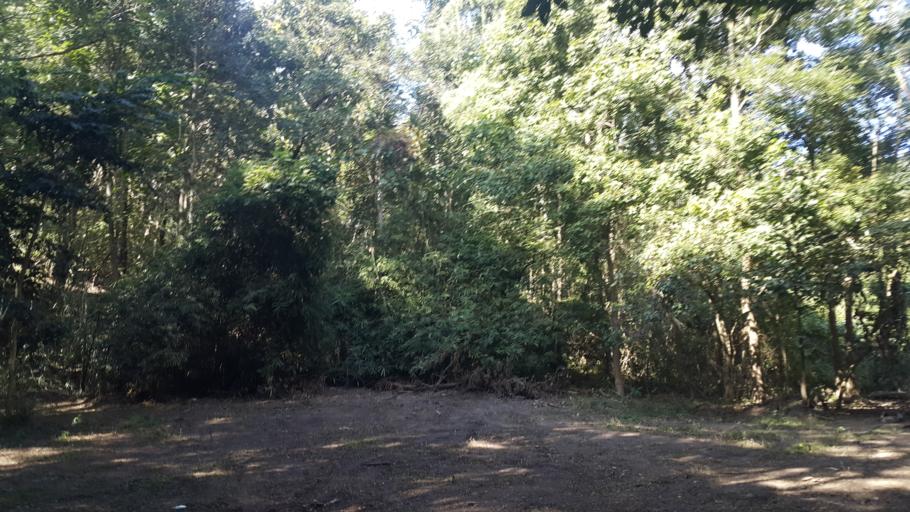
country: TH
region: Lamphun
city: Ban Thi
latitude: 18.5702
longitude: 99.1850
